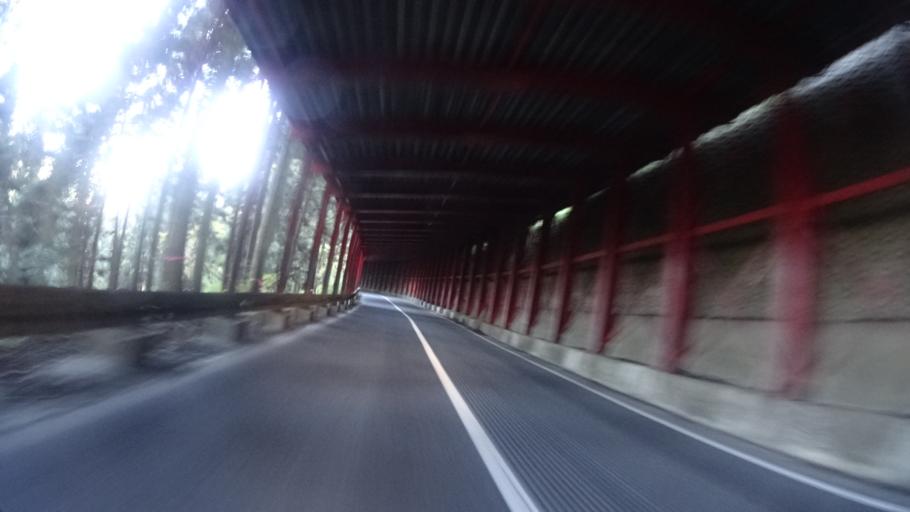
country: JP
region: Fukui
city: Maruoka
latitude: 36.2120
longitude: 136.3508
